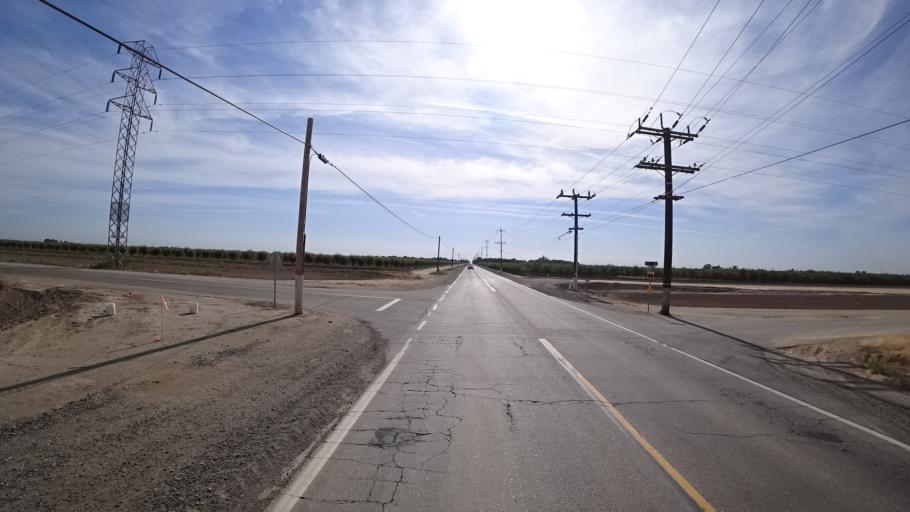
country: US
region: California
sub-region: Kings County
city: Hanford
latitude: 36.3426
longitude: -119.5922
